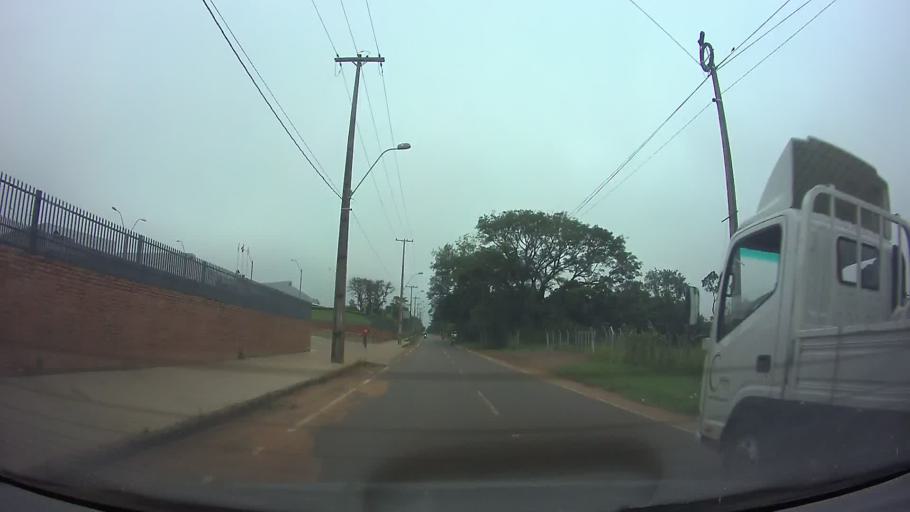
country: PY
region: Central
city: Itaugua
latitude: -25.3811
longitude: -57.3500
